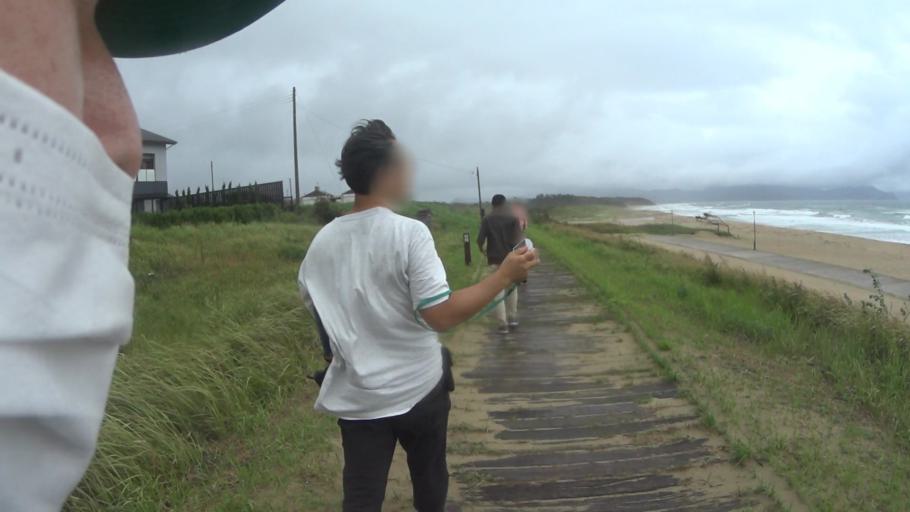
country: JP
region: Hyogo
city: Toyooka
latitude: 35.6623
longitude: 134.9640
